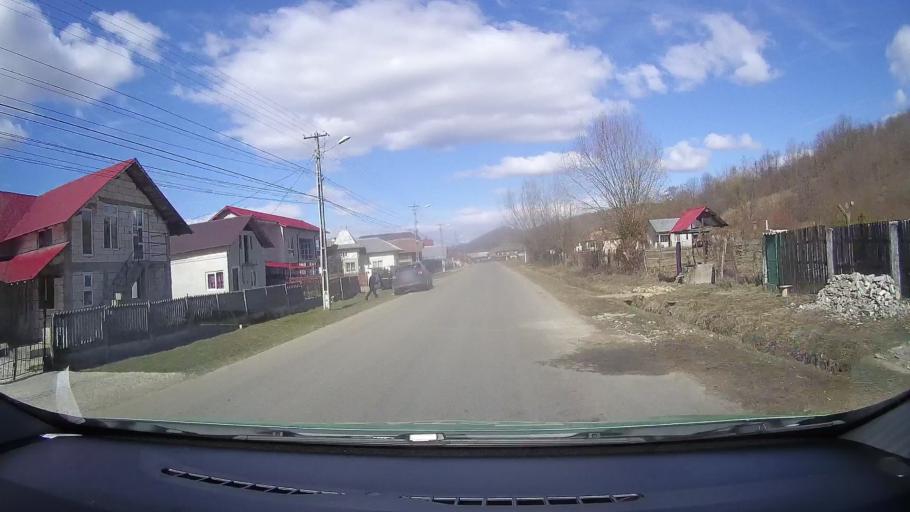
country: RO
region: Dambovita
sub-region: Comuna Vulcana-Pandele
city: Gura Vulcanei
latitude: 45.0333
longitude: 25.3934
